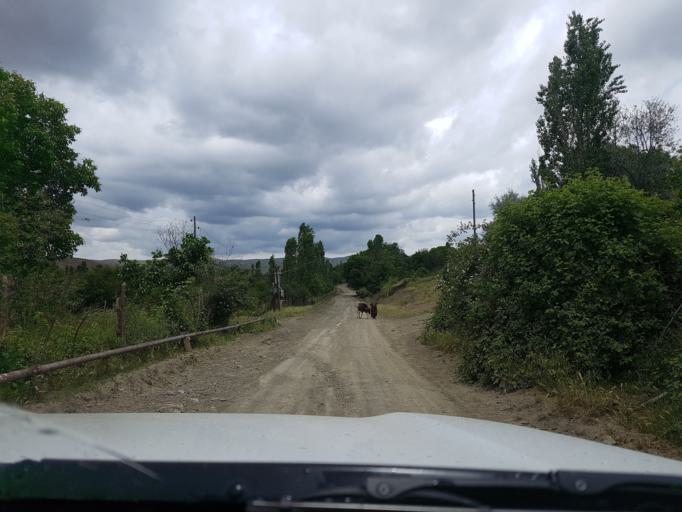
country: TM
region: Ahal
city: Baharly
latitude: 38.1953
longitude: 57.0051
